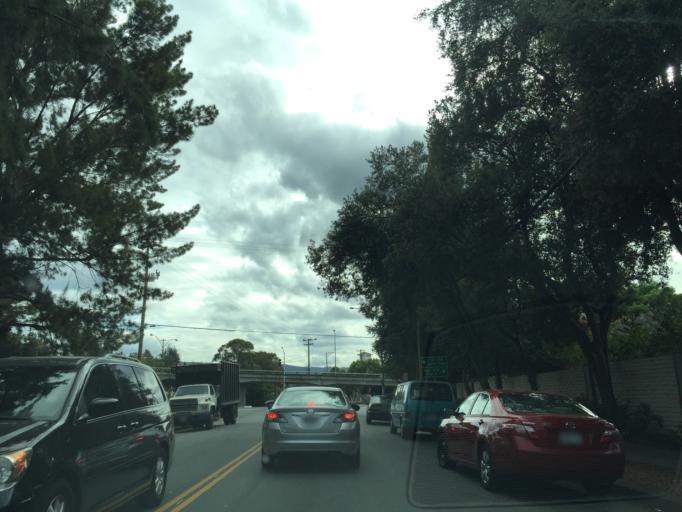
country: US
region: California
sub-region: Santa Clara County
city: Los Altos
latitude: 37.4095
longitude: -122.1083
